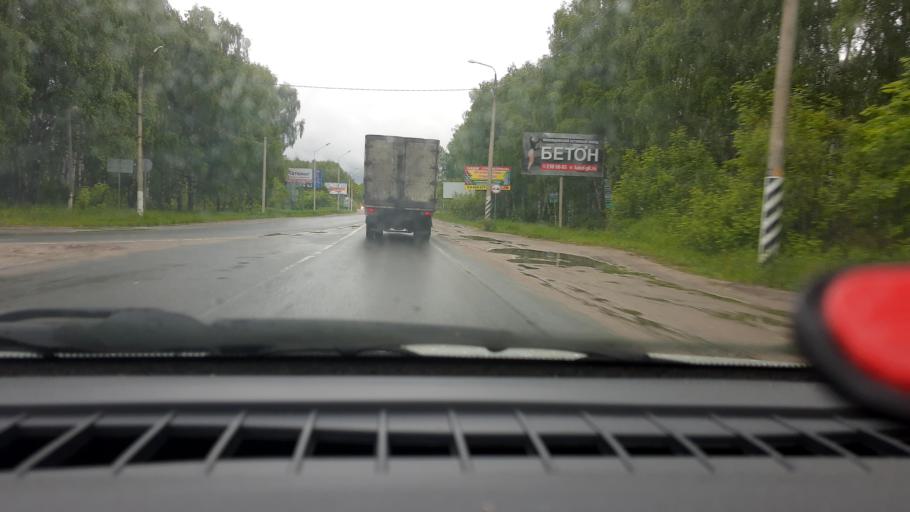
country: RU
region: Nizjnij Novgorod
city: Neklyudovo
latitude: 56.3949
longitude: 44.0094
